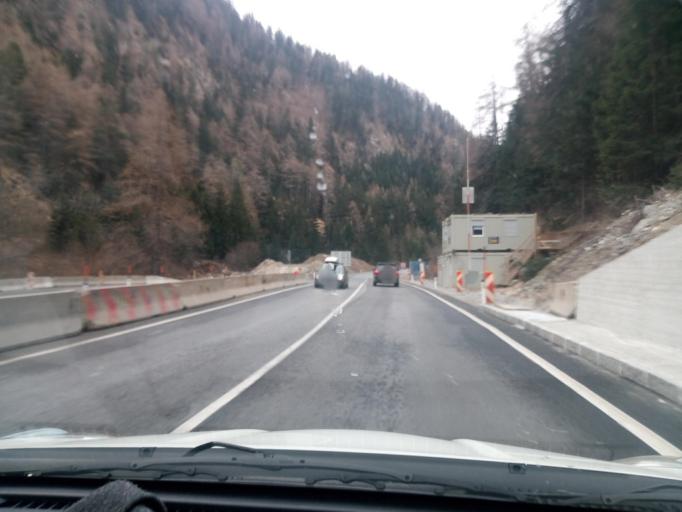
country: AT
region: Tyrol
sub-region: Politischer Bezirk Landeck
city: Nauders
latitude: 46.9107
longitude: 10.4949
